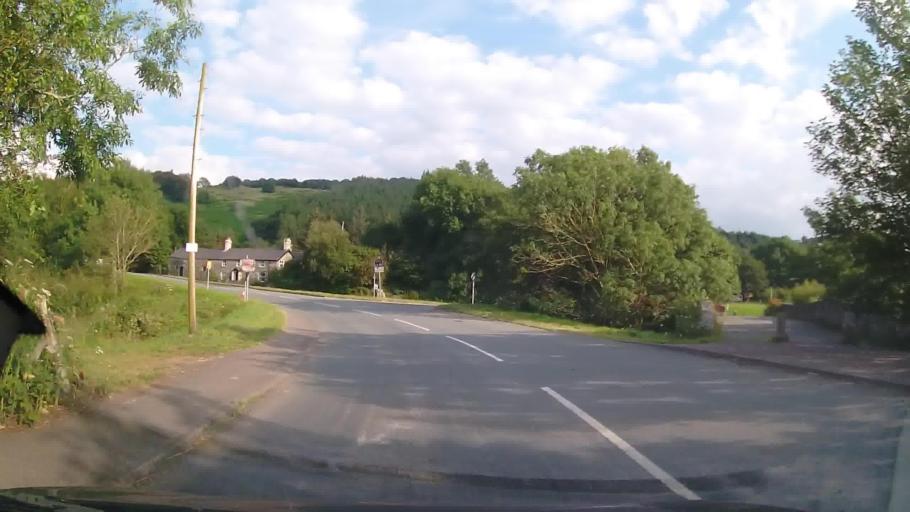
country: GB
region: Wales
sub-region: Gwynedd
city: Bala
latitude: 52.9026
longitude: -3.5928
